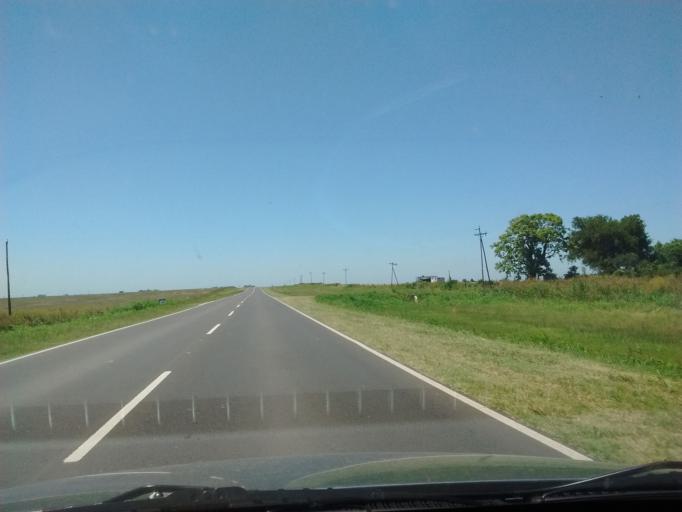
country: AR
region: Entre Rios
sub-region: Departamento de Victoria
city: Victoria
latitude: -32.8052
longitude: -59.8900
